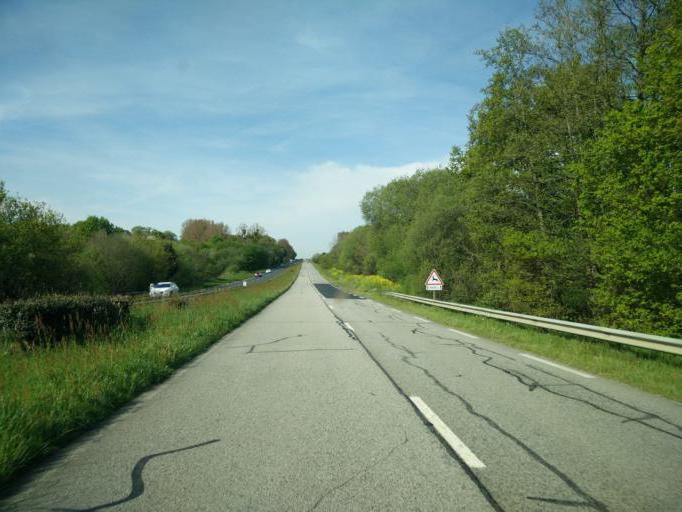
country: FR
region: Lower Normandy
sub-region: Departement de la Manche
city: Le Val-Saint-Pere
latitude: 48.6012
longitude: -1.3964
